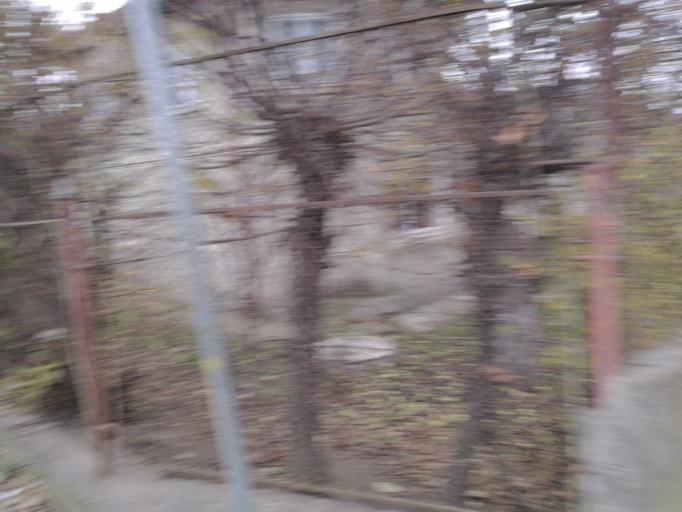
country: RO
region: Suceava
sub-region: Comuna Scheia
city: Scheia
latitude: 47.6742
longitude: 26.2722
